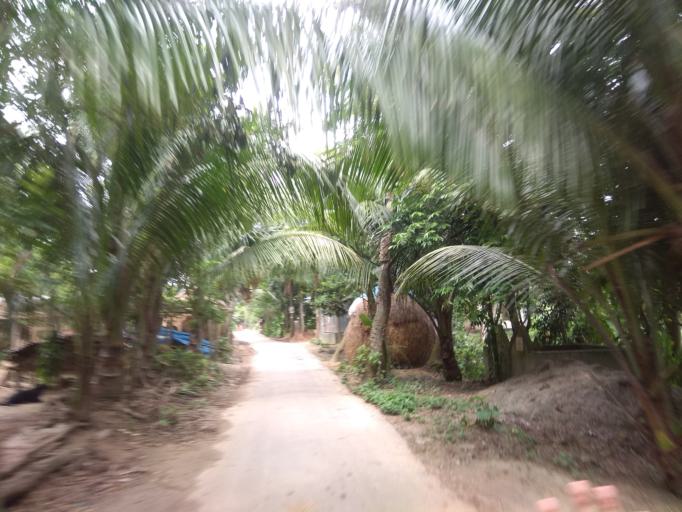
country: BD
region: Dhaka
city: Dohar
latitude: 23.4838
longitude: 90.0161
